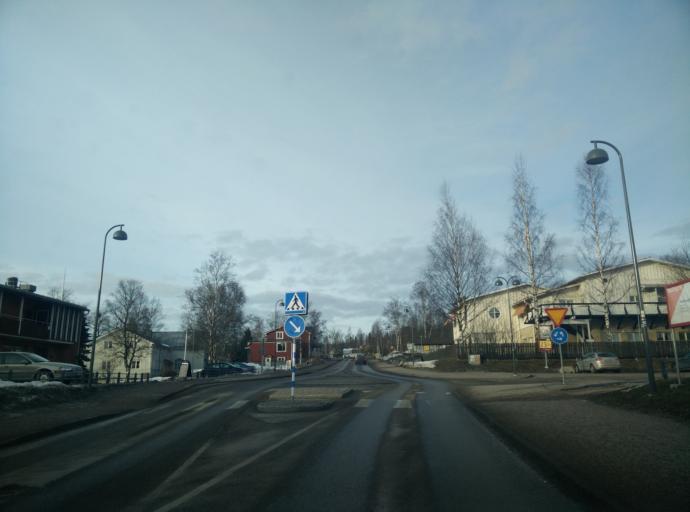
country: SE
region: Vaesternorrland
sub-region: Sundsvalls Kommun
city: Johannedal
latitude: 62.4289
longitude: 17.4163
